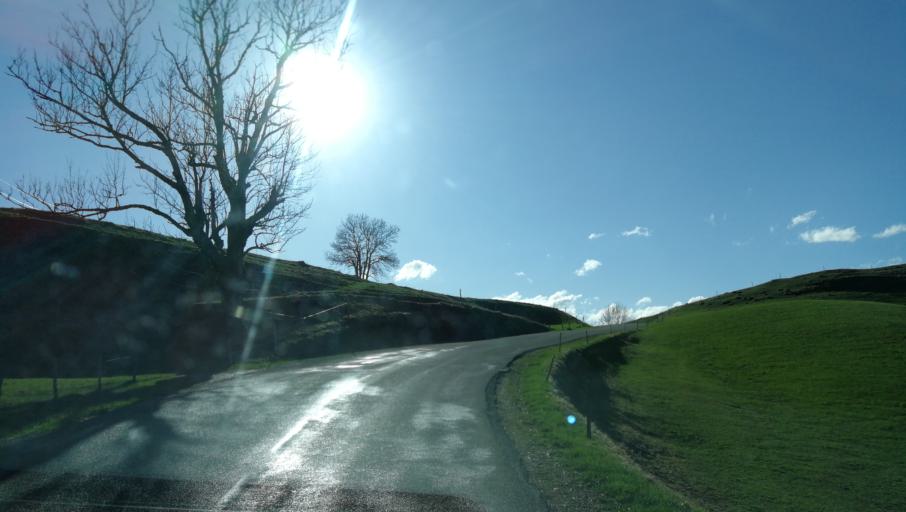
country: FR
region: Franche-Comte
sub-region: Departement du Jura
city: Lavans-les-Saint-Claude
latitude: 46.2660
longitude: 5.8158
